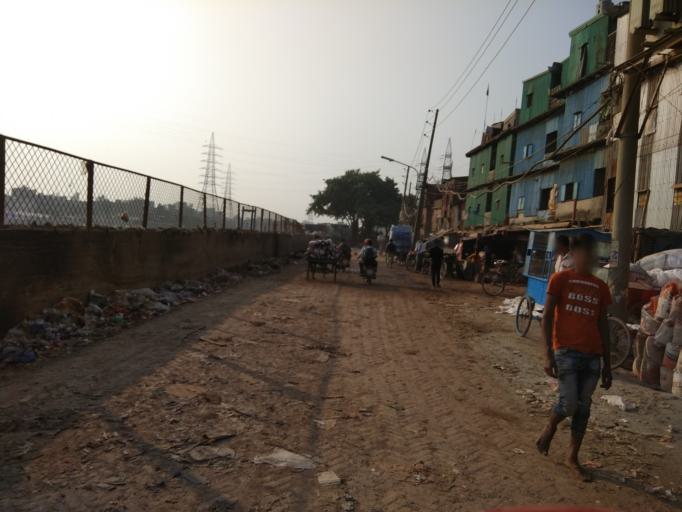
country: BD
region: Dhaka
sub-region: Dhaka
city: Dhaka
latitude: 23.7113
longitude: 90.3922
